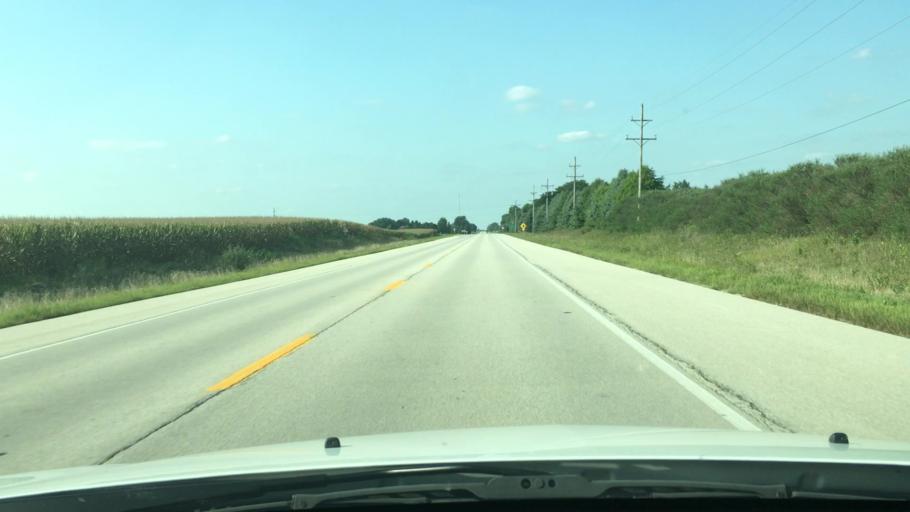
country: US
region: Illinois
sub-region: DeKalb County
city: Waterman
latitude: 41.8459
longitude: -88.7539
